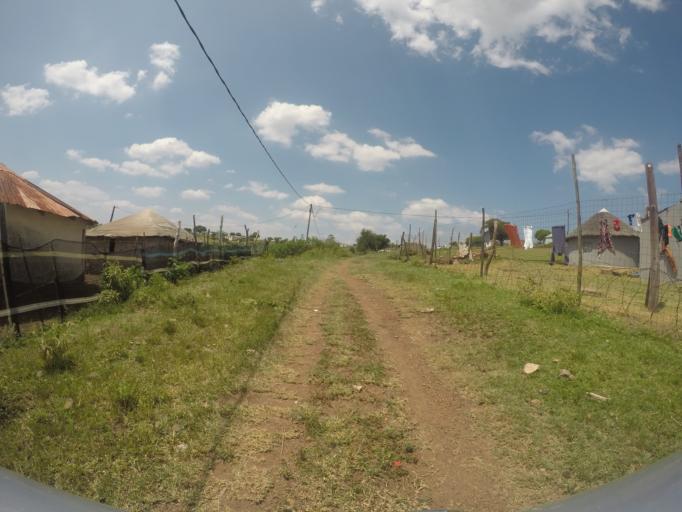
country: ZA
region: KwaZulu-Natal
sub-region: uThungulu District Municipality
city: Empangeni
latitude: -28.5958
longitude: 31.7367
